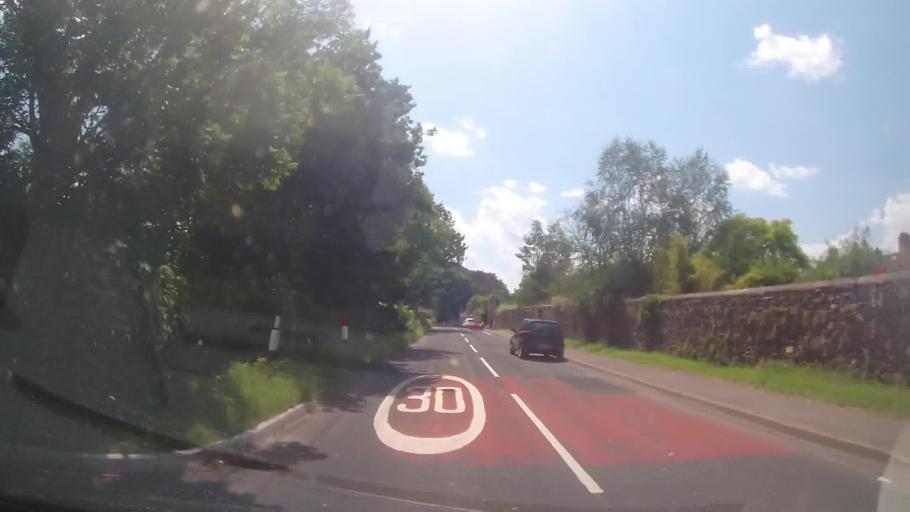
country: GB
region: England
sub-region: Herefordshire
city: Withington
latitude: 52.0345
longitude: -2.6261
